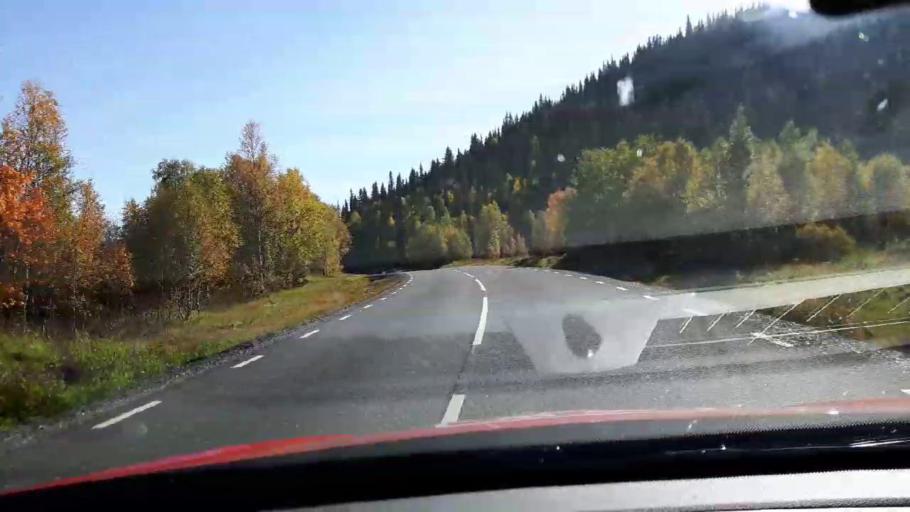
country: NO
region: Nord-Trondelag
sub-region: Royrvik
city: Royrvik
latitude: 64.8338
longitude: 14.0772
